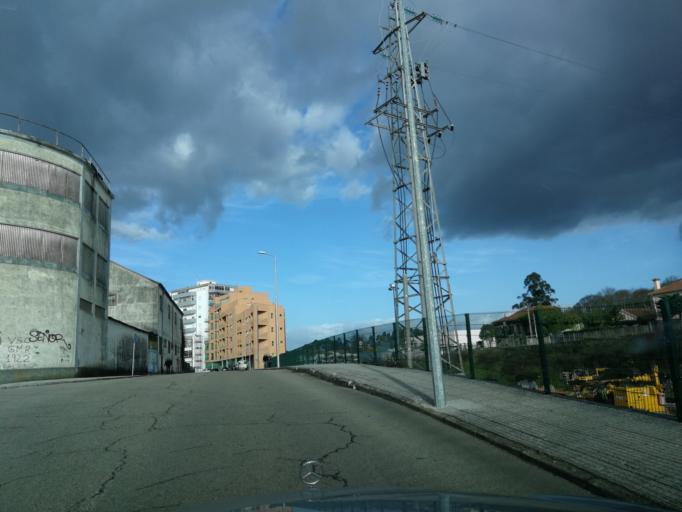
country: PT
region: Viana do Castelo
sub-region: Valenca
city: Valenza
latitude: 42.0257
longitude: -8.6392
